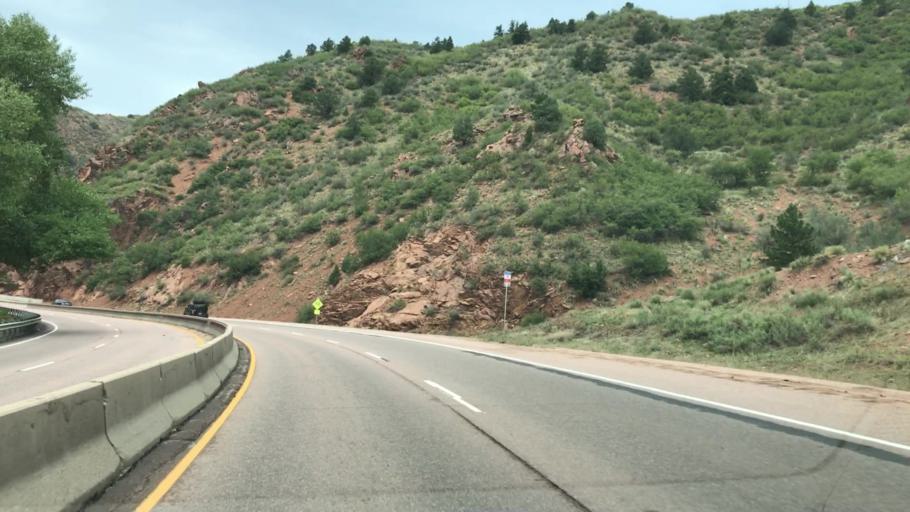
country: US
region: Colorado
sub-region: El Paso County
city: Manitou Springs
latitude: 38.8756
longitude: -104.9296
